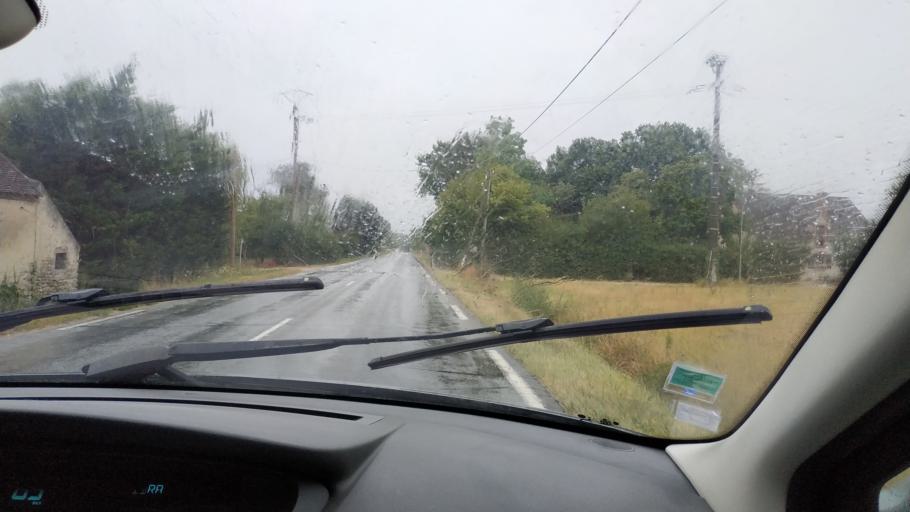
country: FR
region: Centre
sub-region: Departement du Loiret
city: Bellegarde
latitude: 47.9458
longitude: 2.3811
